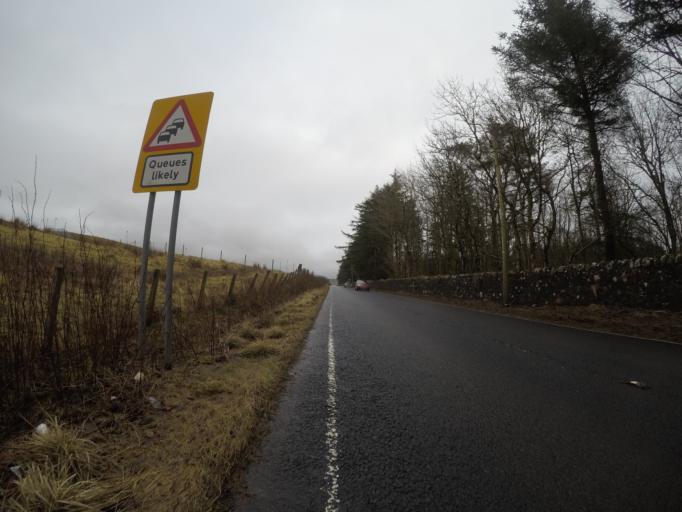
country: GB
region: Scotland
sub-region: North Ayrshire
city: Fairlie
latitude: 55.7757
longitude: -4.8260
